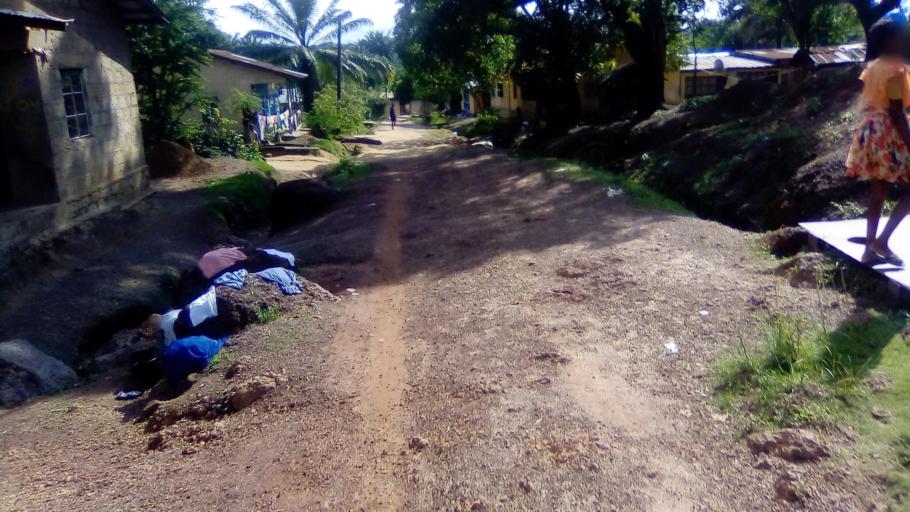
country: SL
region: Southern Province
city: Bo
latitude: 7.9741
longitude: -11.7317
